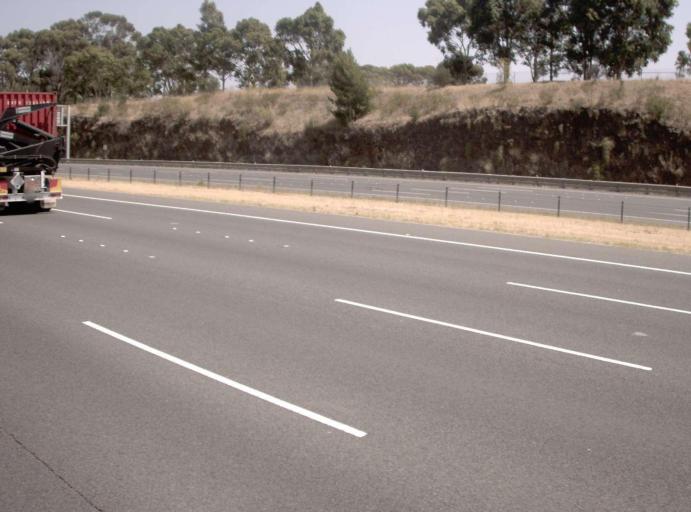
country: AU
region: Victoria
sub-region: Darebin
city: Fairfield
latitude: -37.7917
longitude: 145.0136
